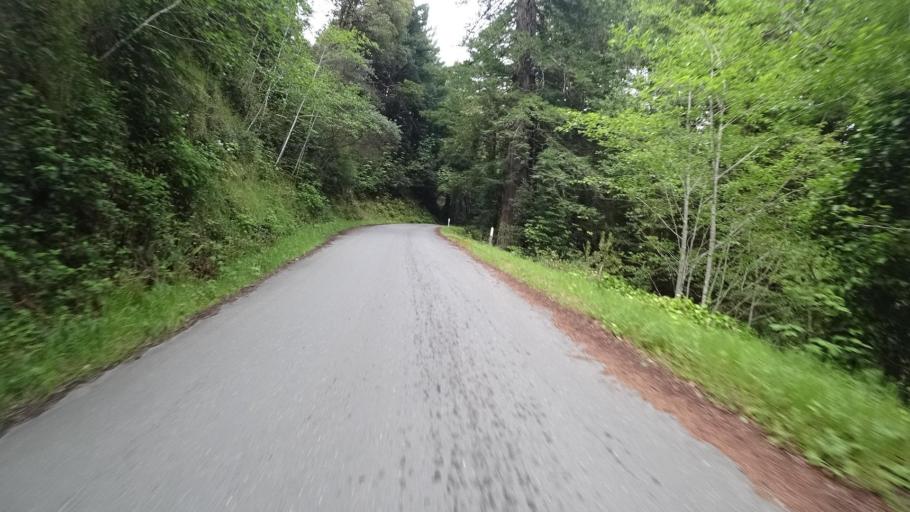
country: US
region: California
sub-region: Humboldt County
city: Redway
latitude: 40.3364
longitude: -123.9073
